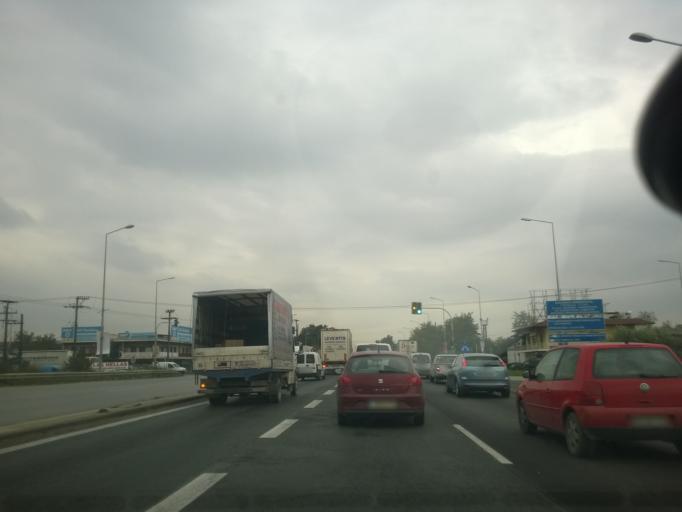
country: GR
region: Central Macedonia
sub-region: Nomos Thessalonikis
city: Nea Magnisia
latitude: 40.7018
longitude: 22.8210
